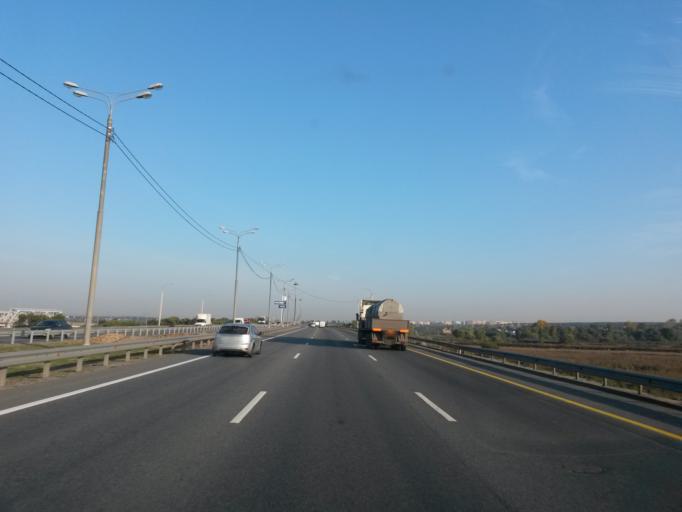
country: RU
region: Moskovskaya
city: Yam
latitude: 55.4933
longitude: 37.7342
